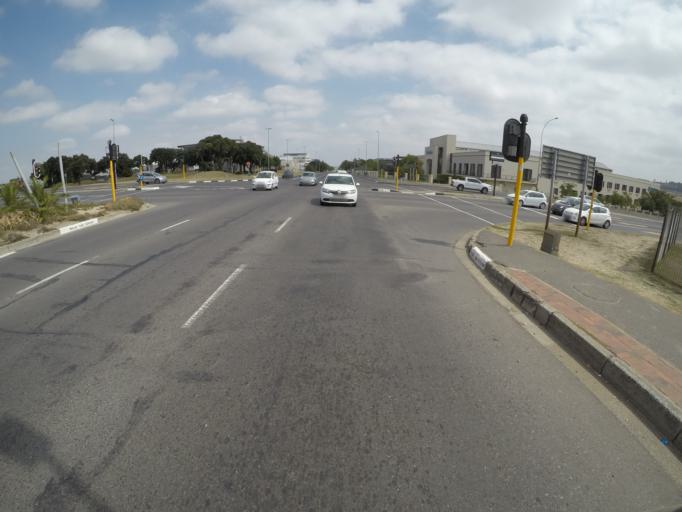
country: ZA
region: Western Cape
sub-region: City of Cape Town
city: Kraaifontein
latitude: -33.8768
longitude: 18.6363
